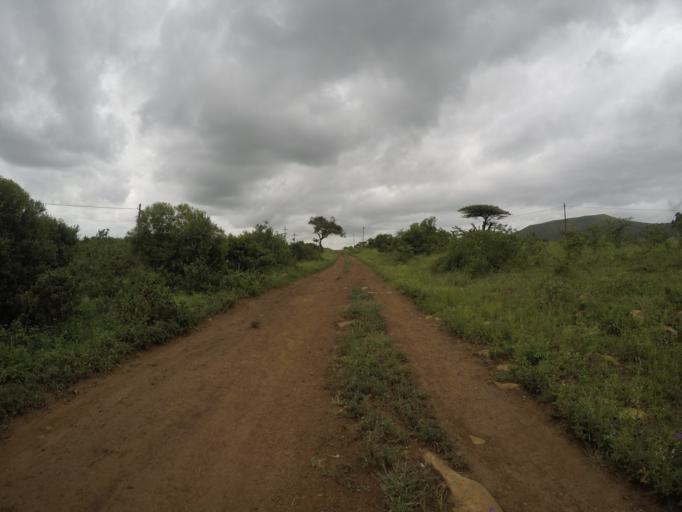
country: ZA
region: KwaZulu-Natal
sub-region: uThungulu District Municipality
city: Empangeni
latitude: -28.5868
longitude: 31.8629
